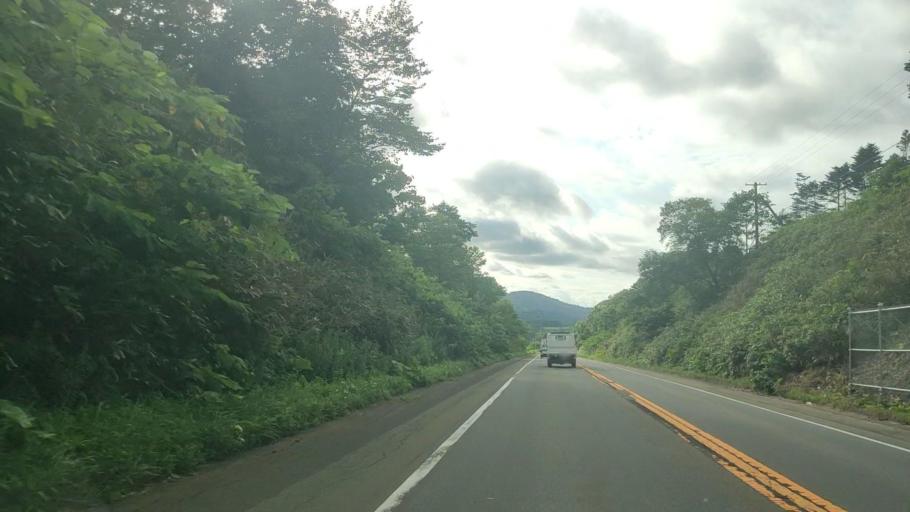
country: JP
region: Hokkaido
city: Niseko Town
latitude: 42.5982
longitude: 140.5004
